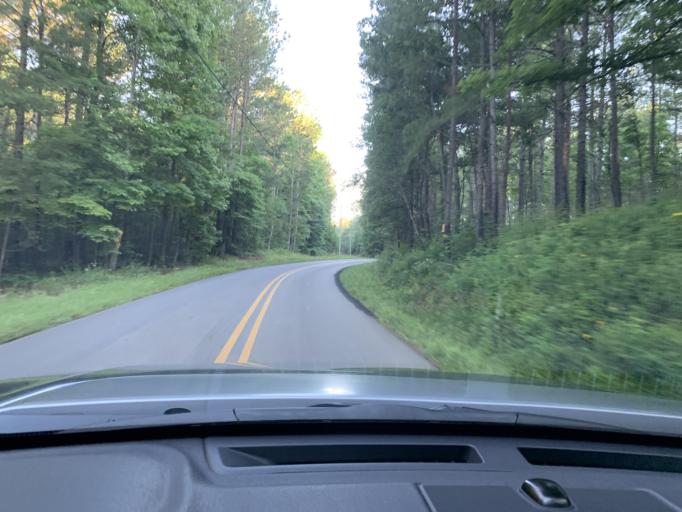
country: US
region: Georgia
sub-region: Bartow County
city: Rydal
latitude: 34.2551
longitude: -84.6903
